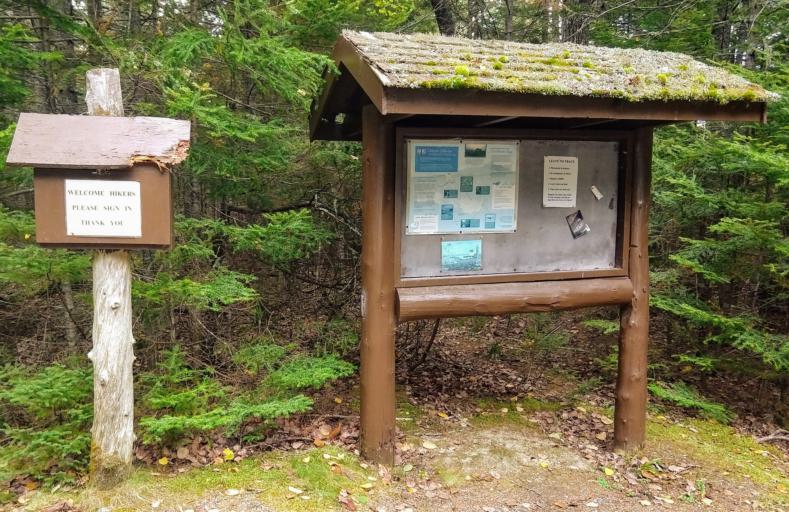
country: US
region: Maine
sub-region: Washington County
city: Eastport
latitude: 44.8393
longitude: -67.1883
